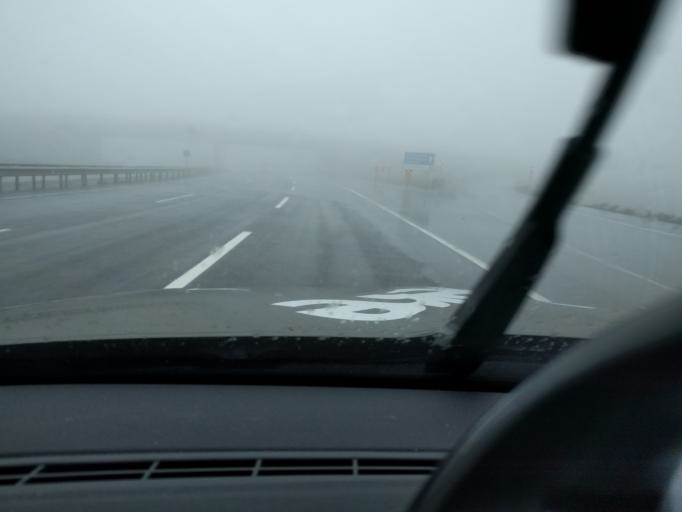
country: TR
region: Istanbul
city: Boyalik
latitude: 41.2487
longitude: 28.5875
